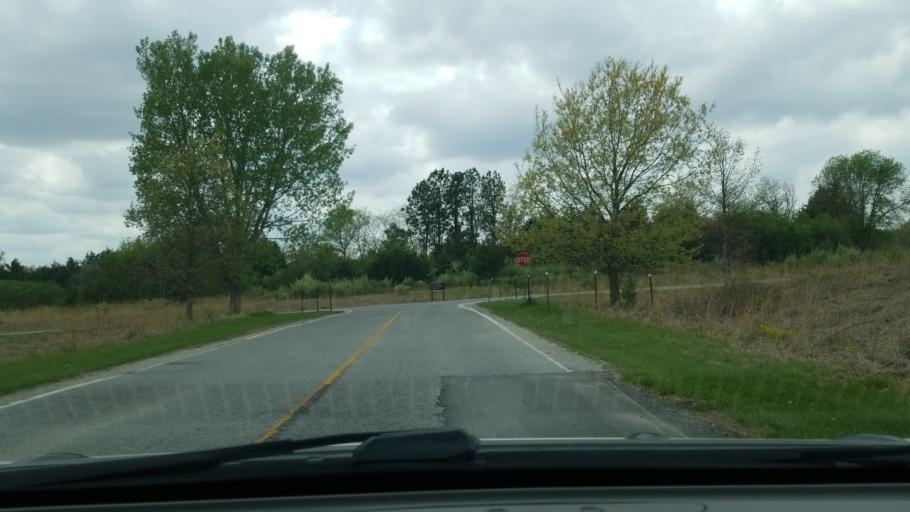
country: US
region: Nebraska
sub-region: Sarpy County
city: Chalco
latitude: 41.1654
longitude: -96.1629
